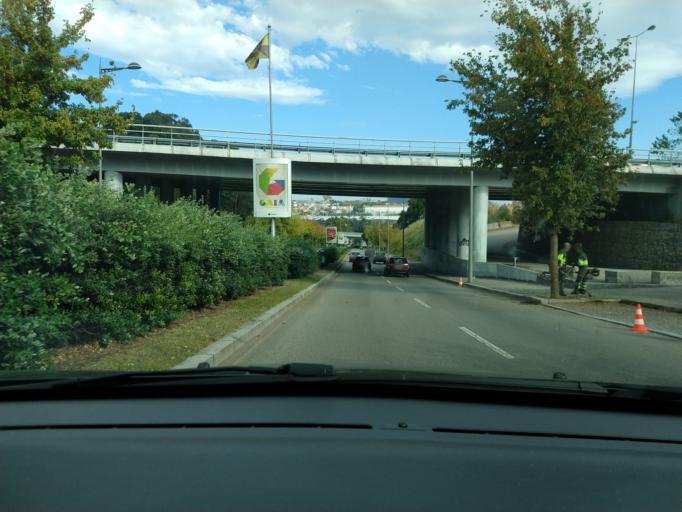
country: PT
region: Porto
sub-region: Vila Nova de Gaia
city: Oliveira do Douro
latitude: 41.1273
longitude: -8.5981
